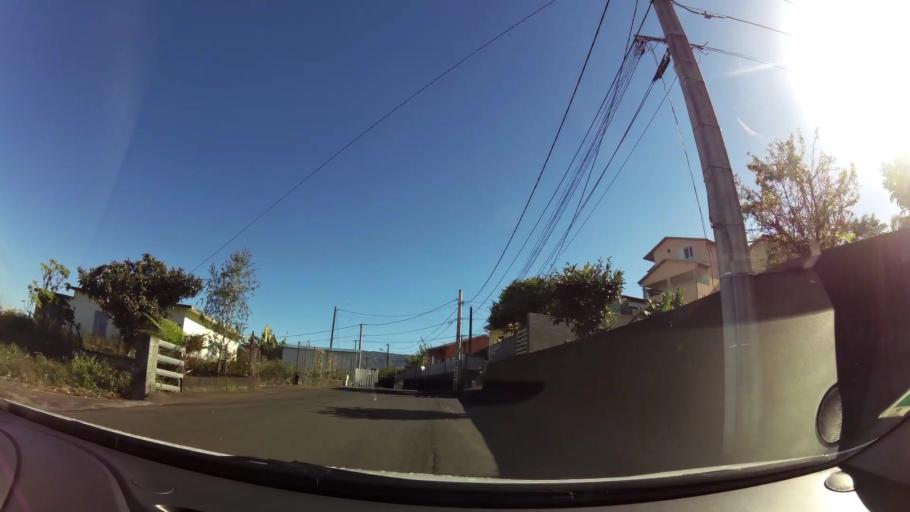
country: RE
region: Reunion
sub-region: Reunion
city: Le Tampon
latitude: -21.2384
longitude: 55.5268
